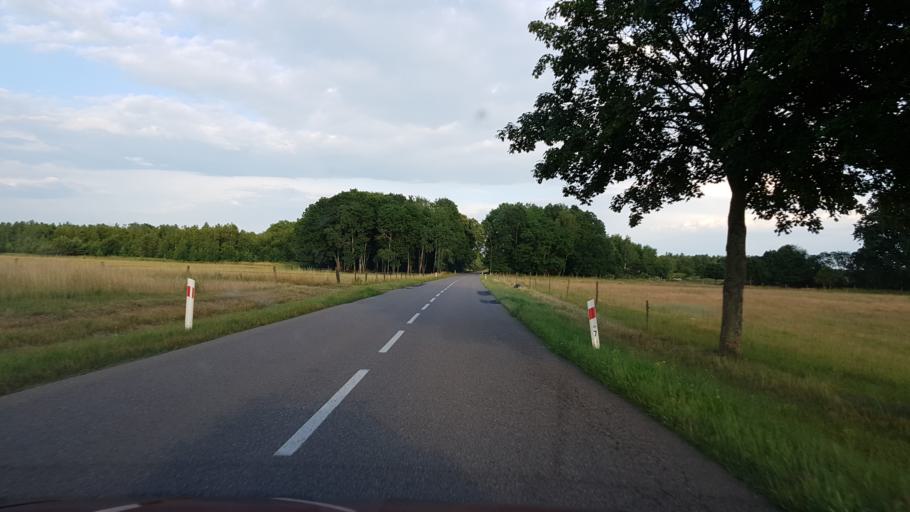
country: PL
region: West Pomeranian Voivodeship
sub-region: Powiat goleniowski
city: Nowogard
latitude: 53.6957
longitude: 15.0615
